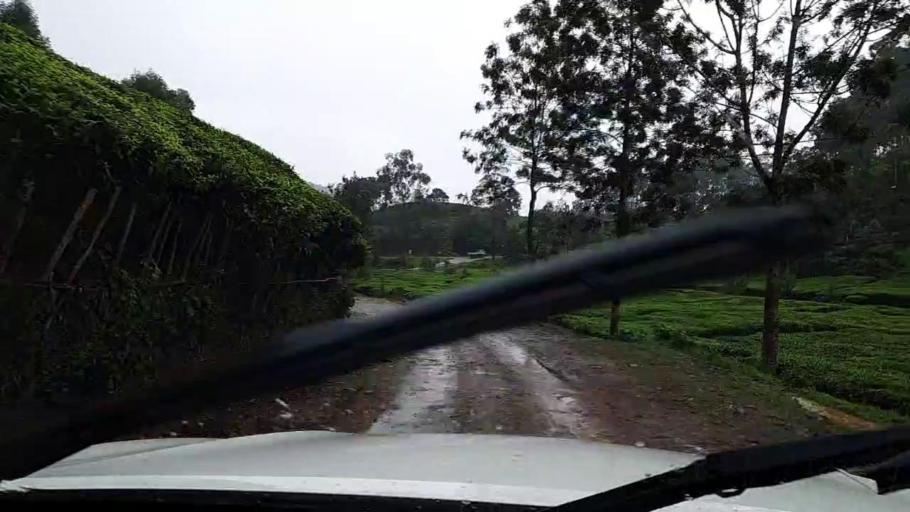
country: RW
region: Western Province
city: Cyangugu
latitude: -2.4491
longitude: 29.0375
